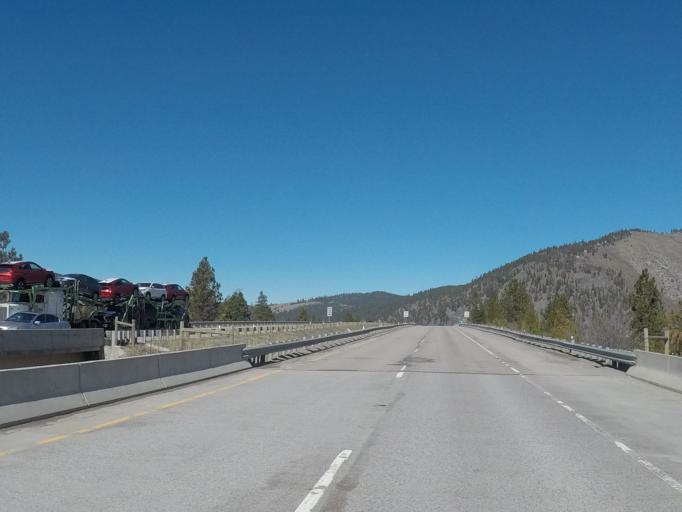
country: US
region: Montana
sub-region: Missoula County
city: Bonner-West Riverside
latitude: 46.8720
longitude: -113.8870
